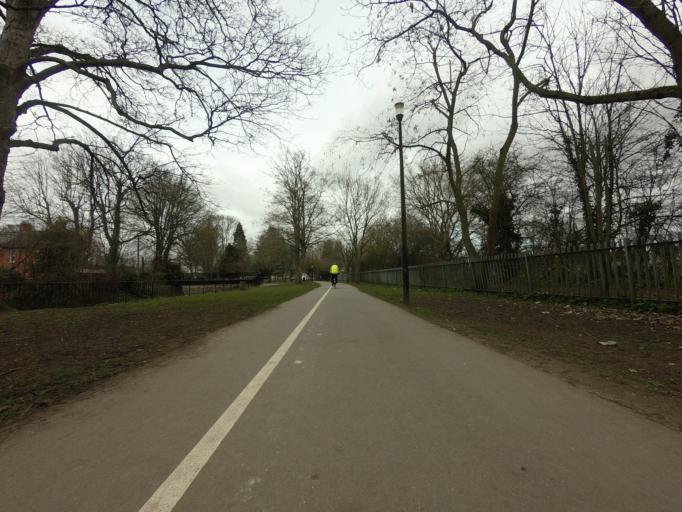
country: GB
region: England
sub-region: Lincolnshire
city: Grantham
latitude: 52.9161
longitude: -0.6372
